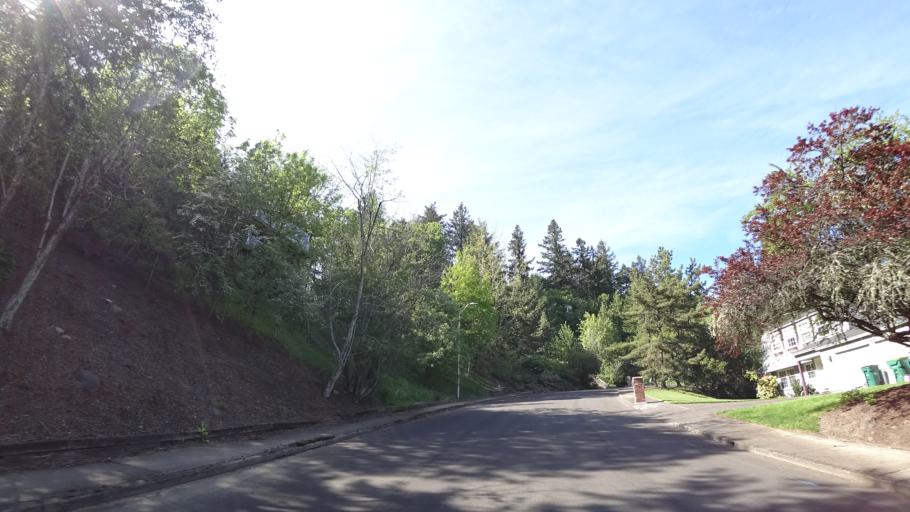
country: US
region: Oregon
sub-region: Washington County
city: West Slope
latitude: 45.4985
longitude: -122.7473
